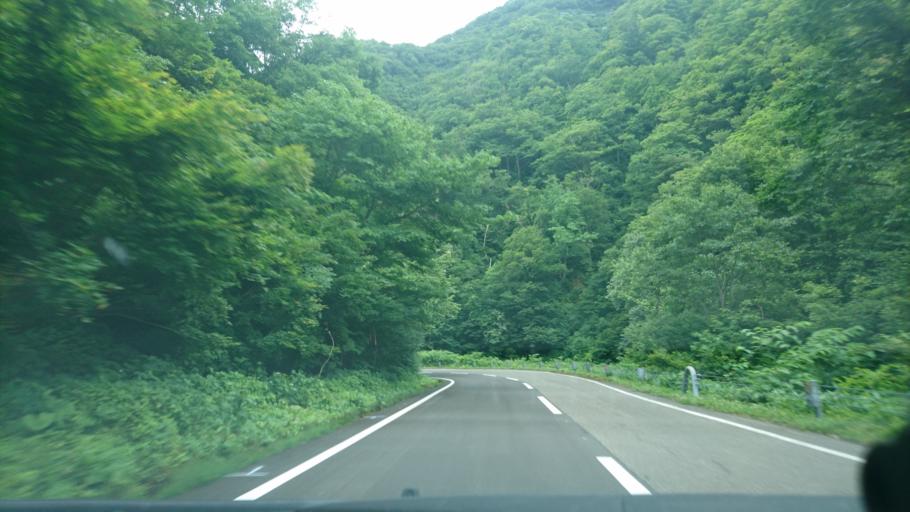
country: JP
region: Akita
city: Yuzawa
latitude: 39.1665
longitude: 140.7441
